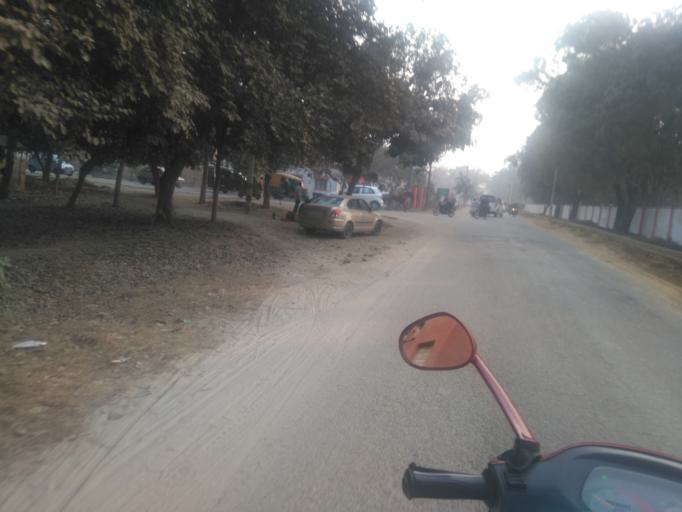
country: IN
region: Uttar Pradesh
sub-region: Meerut
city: Meerut
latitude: 28.9879
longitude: 77.6773
